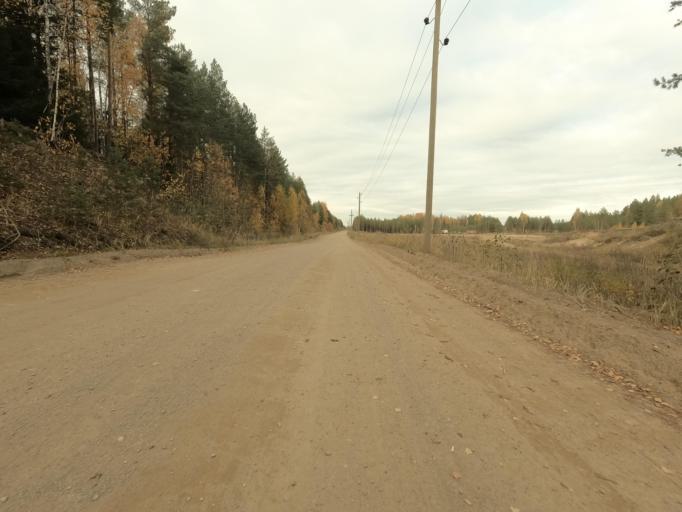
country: RU
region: Leningrad
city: Priladozhskiy
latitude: 59.6930
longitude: 31.3612
